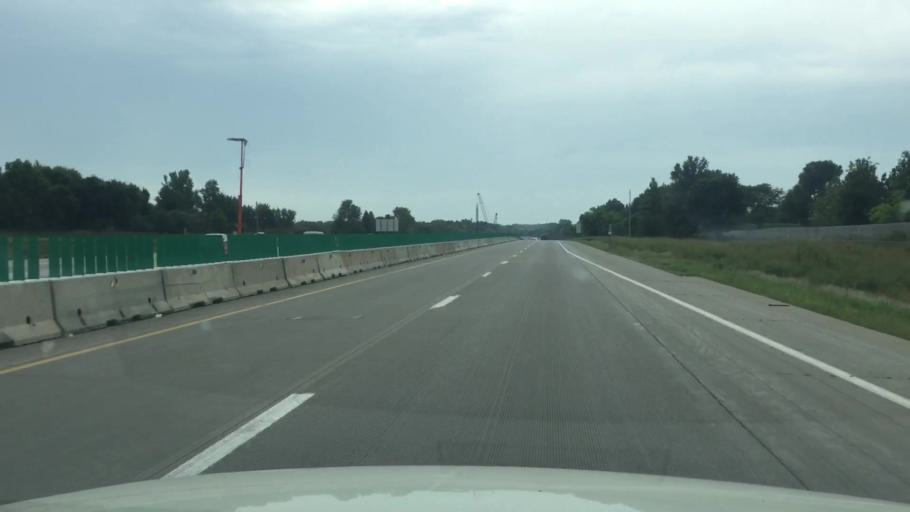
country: US
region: Iowa
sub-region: Polk County
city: Ankeny
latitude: 41.7527
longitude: -93.5729
